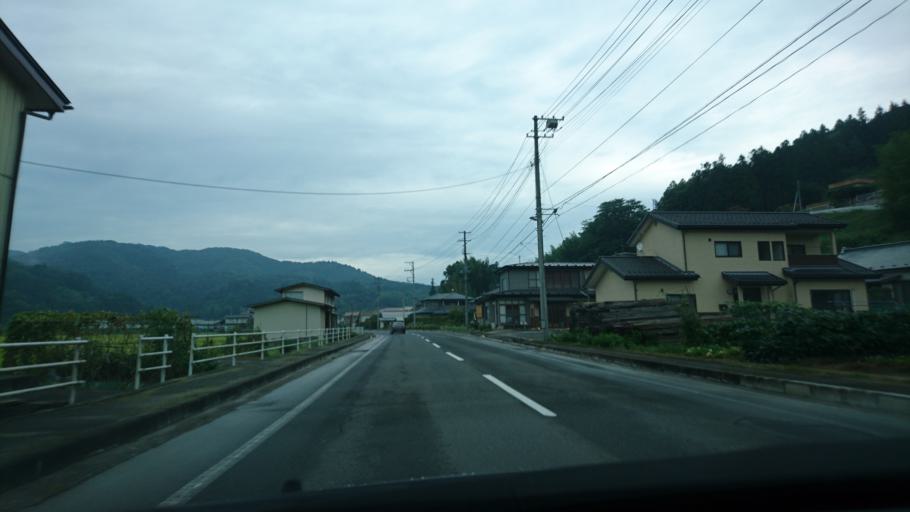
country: JP
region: Iwate
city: Ichinoseki
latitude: 38.9736
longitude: 141.2434
